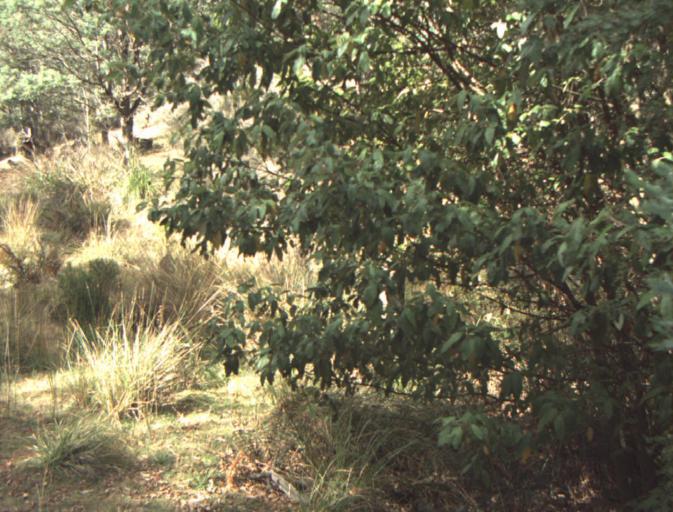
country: AU
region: Tasmania
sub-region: Launceston
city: Mayfield
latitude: -41.2806
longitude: 147.2327
